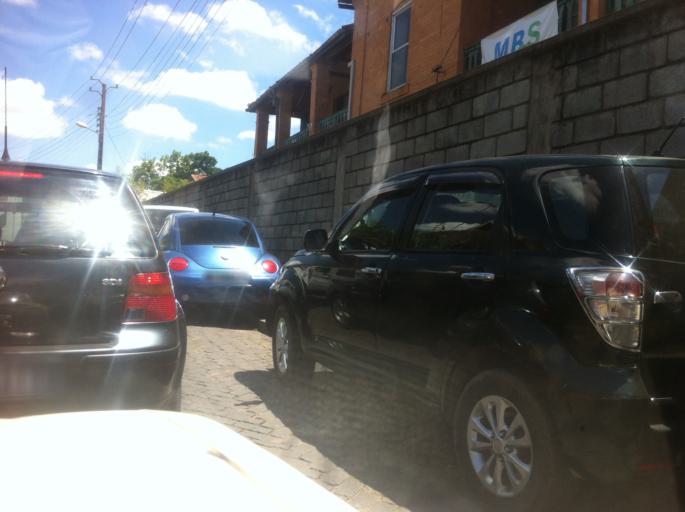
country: MG
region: Analamanga
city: Antananarivo
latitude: -18.9124
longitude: 47.5270
